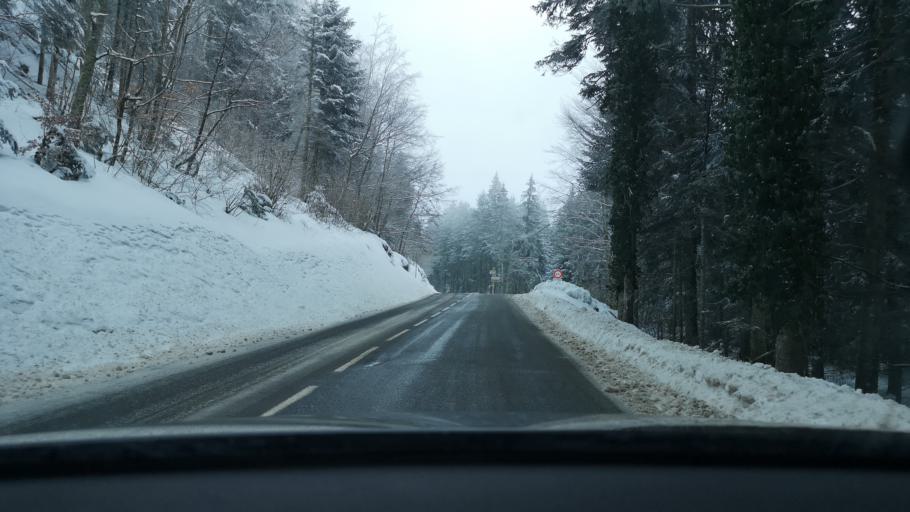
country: FR
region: Rhone-Alpes
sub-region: Departement de l'Ain
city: Oyonnax
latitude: 46.2379
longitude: 5.7021
